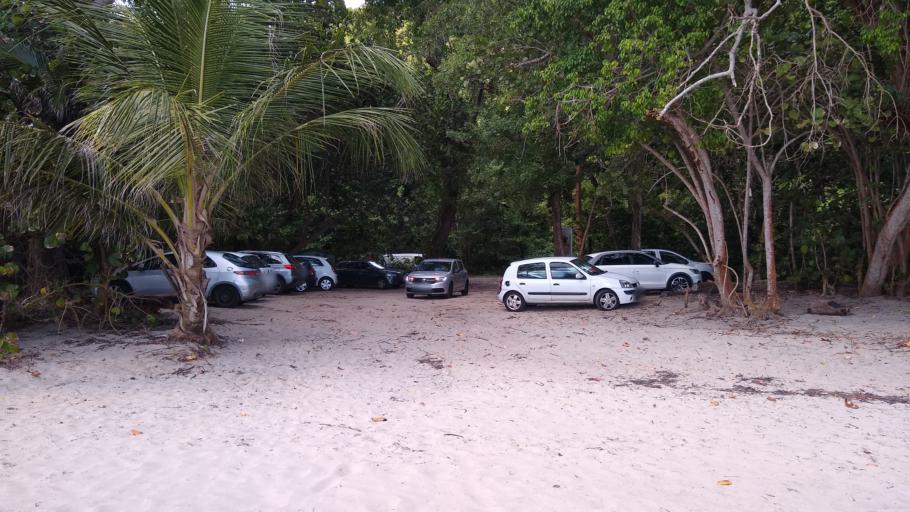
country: MQ
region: Martinique
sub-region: Martinique
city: Les Trois-Ilets
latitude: 14.4737
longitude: -61.0407
